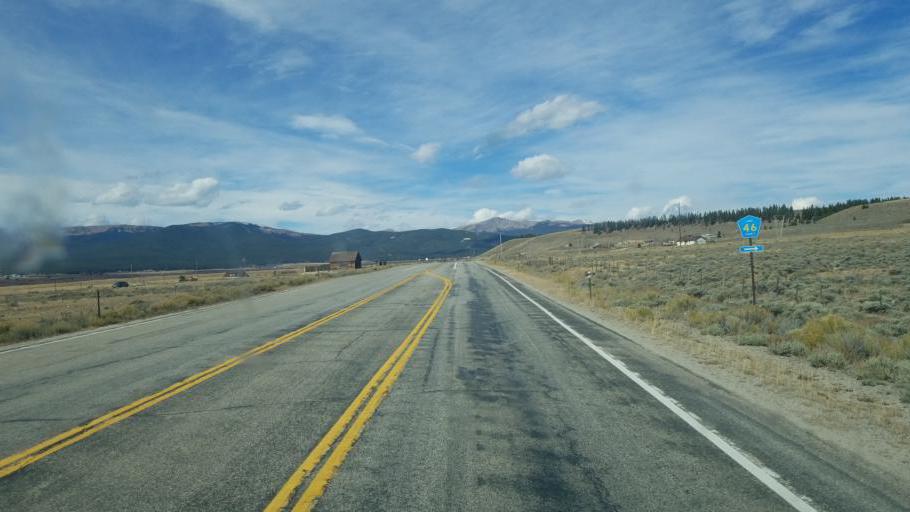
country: US
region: Colorado
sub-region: Lake County
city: Leadville
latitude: 39.1906
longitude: -106.3328
